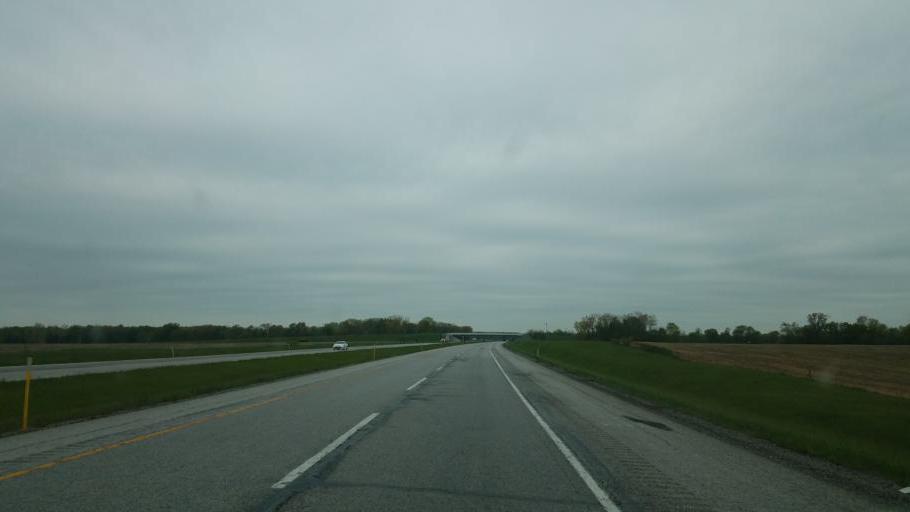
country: US
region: Michigan
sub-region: Saint Joseph County
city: White Pigeon
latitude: 41.7491
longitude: -85.5570
